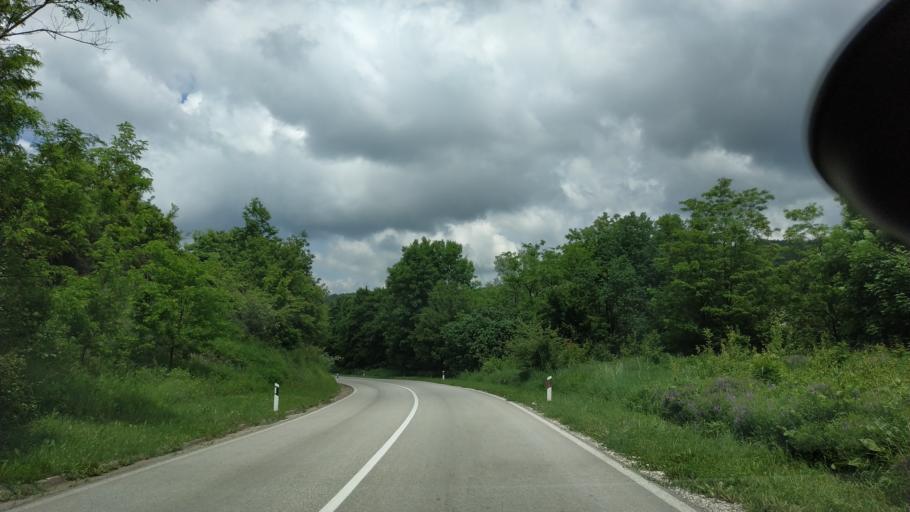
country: RS
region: Central Serbia
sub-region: Borski Okrug
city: Bor
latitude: 44.0662
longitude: 22.0364
